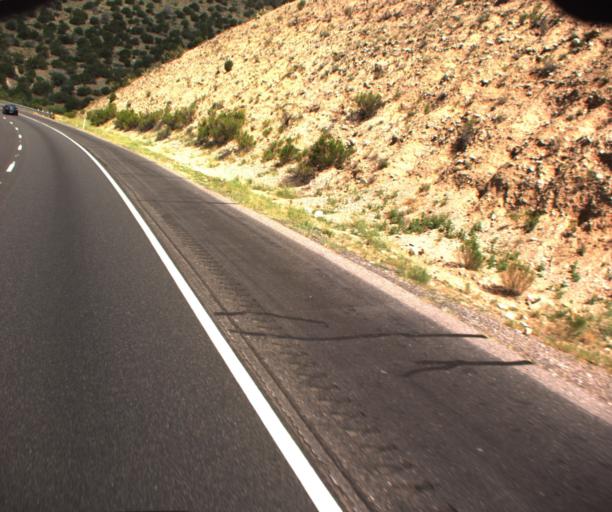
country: US
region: Arizona
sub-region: Yavapai County
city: Camp Verde
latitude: 34.5388
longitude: -111.9217
